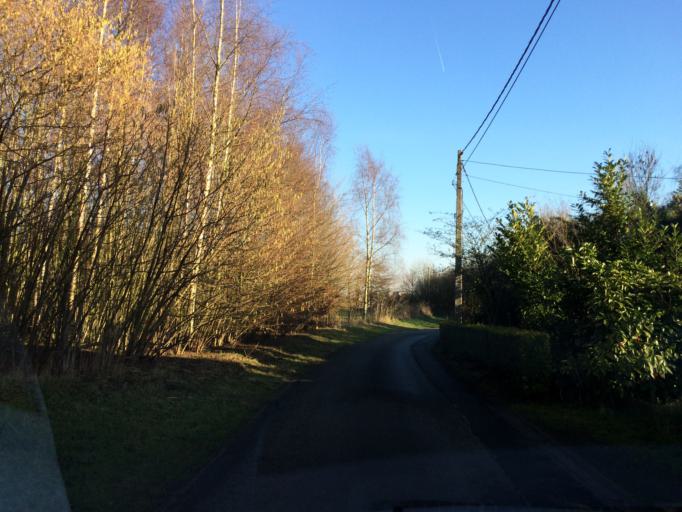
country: BE
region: Flanders
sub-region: Provincie West-Vlaanderen
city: Roeselare
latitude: 50.9211
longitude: 3.1368
